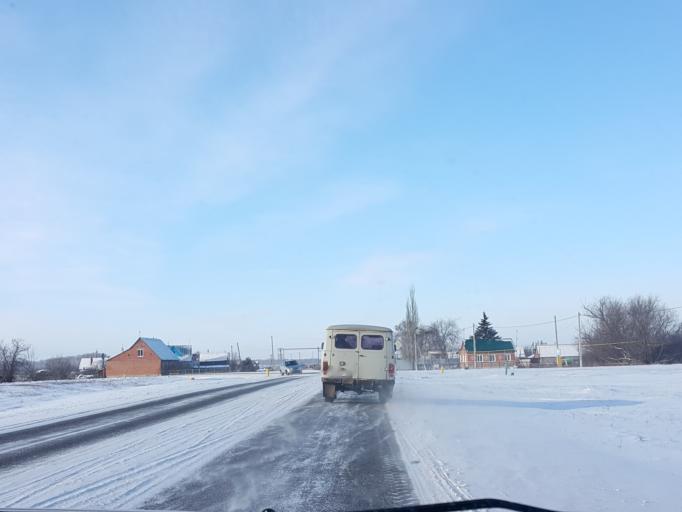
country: RU
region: Tambov
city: Znamenka
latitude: 52.4132
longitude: 41.4224
